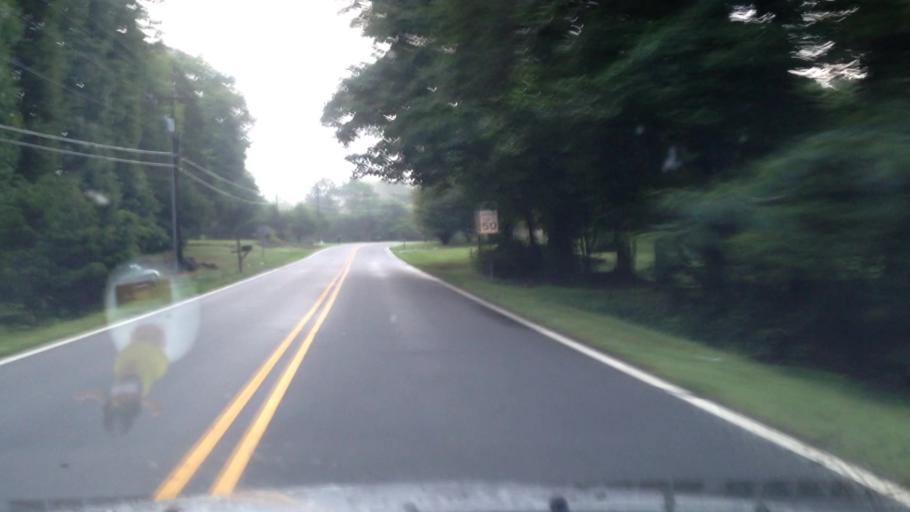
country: US
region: North Carolina
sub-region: Forsyth County
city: Kernersville
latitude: 36.1512
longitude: -80.0906
